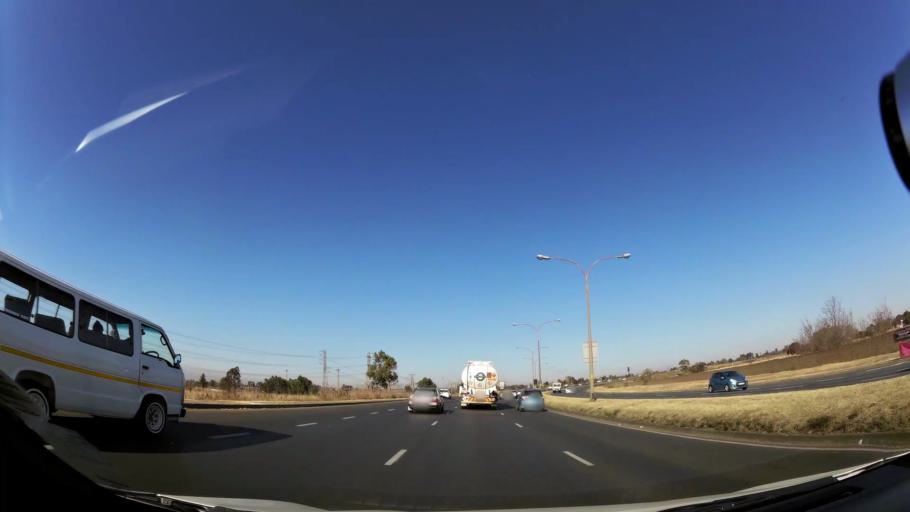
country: ZA
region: Gauteng
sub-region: Ekurhuleni Metropolitan Municipality
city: Germiston
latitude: -26.3023
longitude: 28.1168
